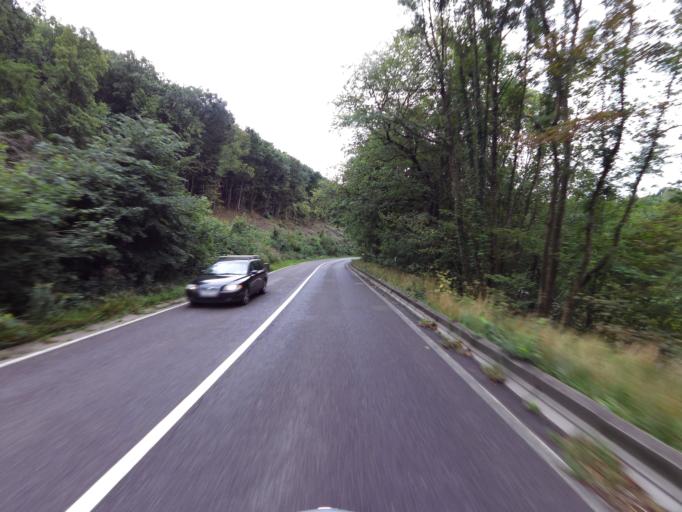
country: BE
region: Wallonia
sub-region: Province de Namur
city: Rochefort
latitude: 50.1458
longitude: 5.1944
